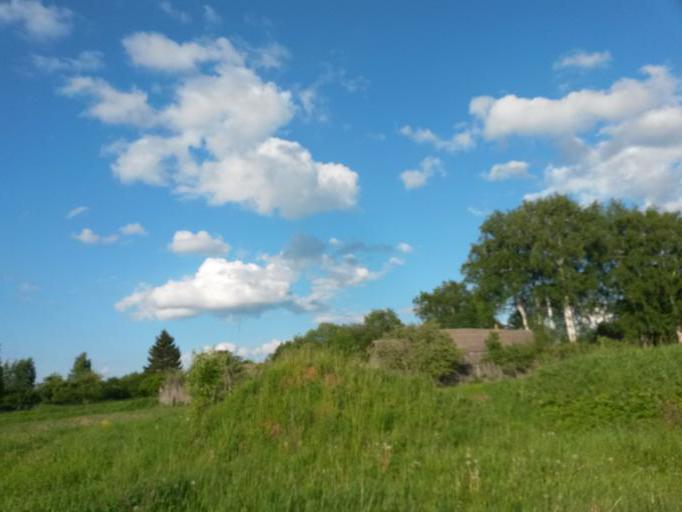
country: RU
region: Jaroslavl
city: Burmakino
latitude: 57.3614
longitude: 40.1986
